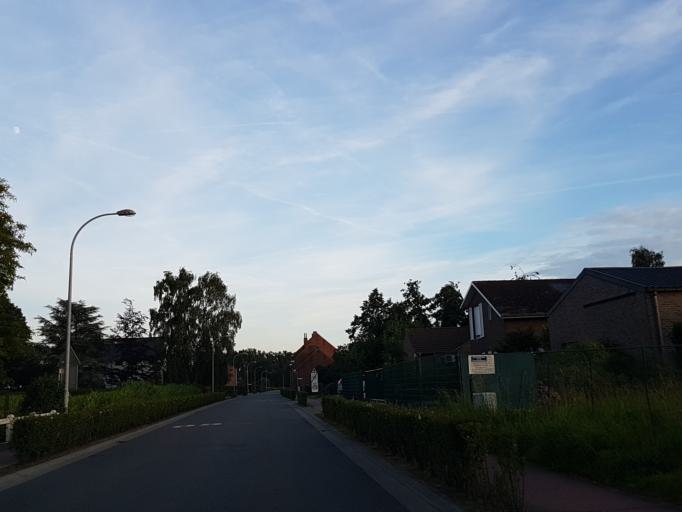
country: BE
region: Flanders
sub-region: Provincie Vlaams-Brabant
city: Londerzeel
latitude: 51.0011
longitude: 4.2849
